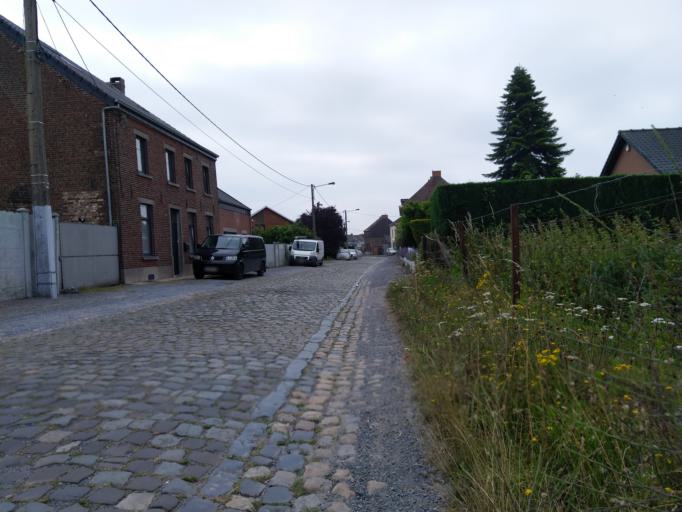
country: BE
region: Wallonia
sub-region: Province du Hainaut
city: Jurbise
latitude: 50.4850
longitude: 3.9119
